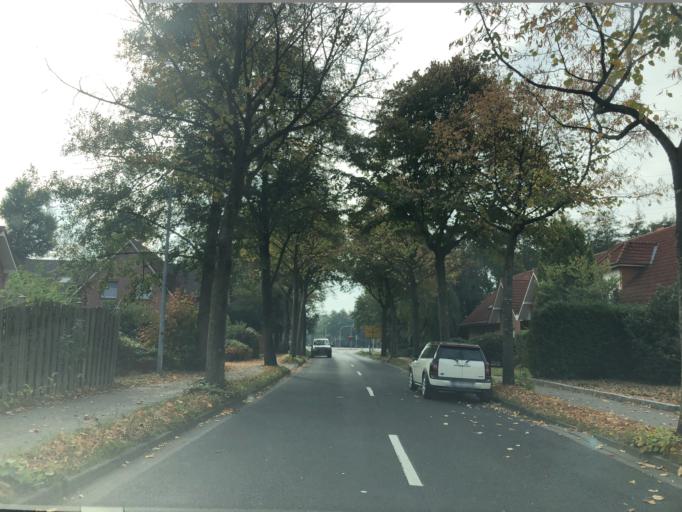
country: DE
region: Lower Saxony
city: Papenburg
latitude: 53.0686
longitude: 7.3955
